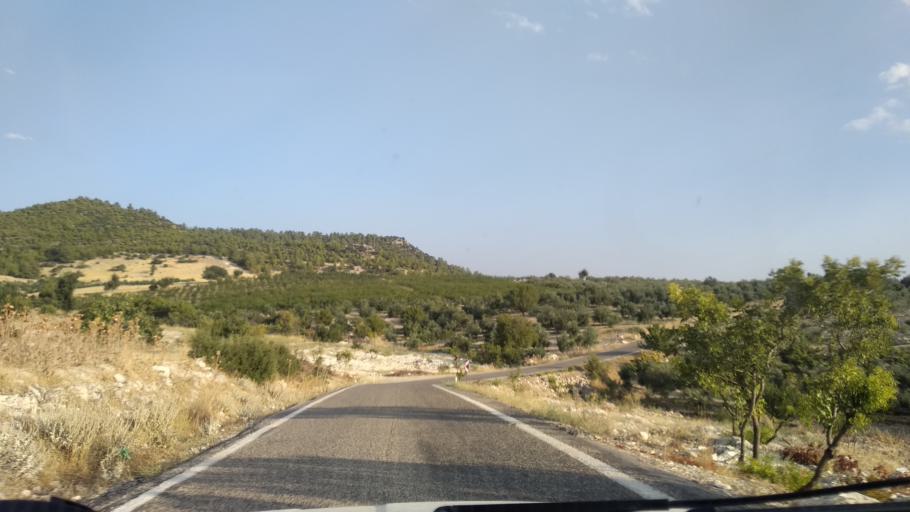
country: TR
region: Mersin
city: Sarikavak
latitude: 36.5674
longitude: 33.6335
